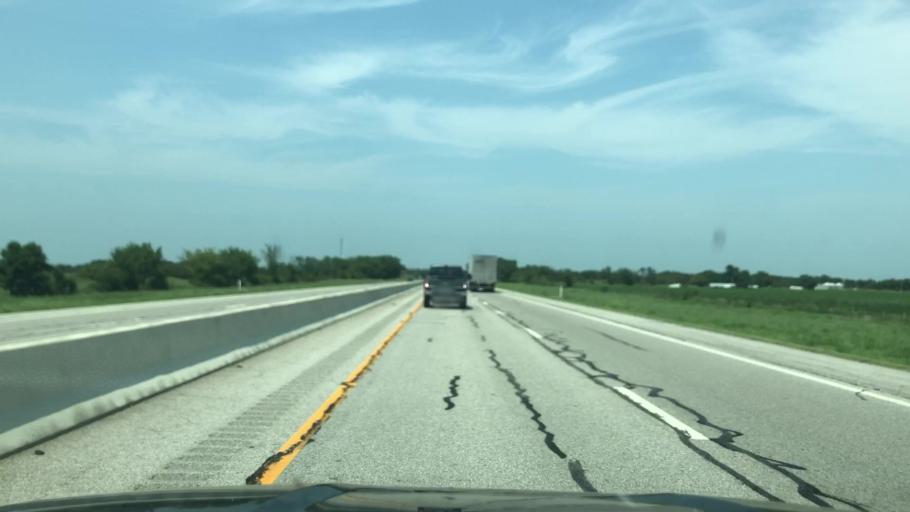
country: US
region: Oklahoma
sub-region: Ottawa County
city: Fairland
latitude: 36.7673
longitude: -94.8960
